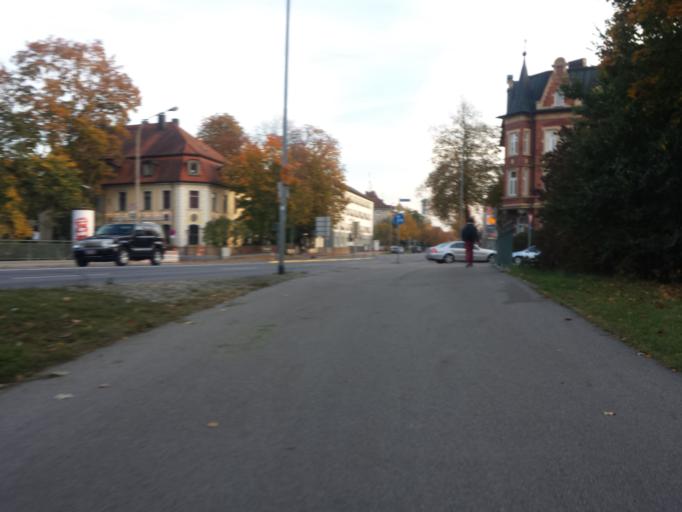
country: DE
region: Bavaria
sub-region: Upper Bavaria
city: Ingolstadt
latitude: 48.7551
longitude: 11.4306
